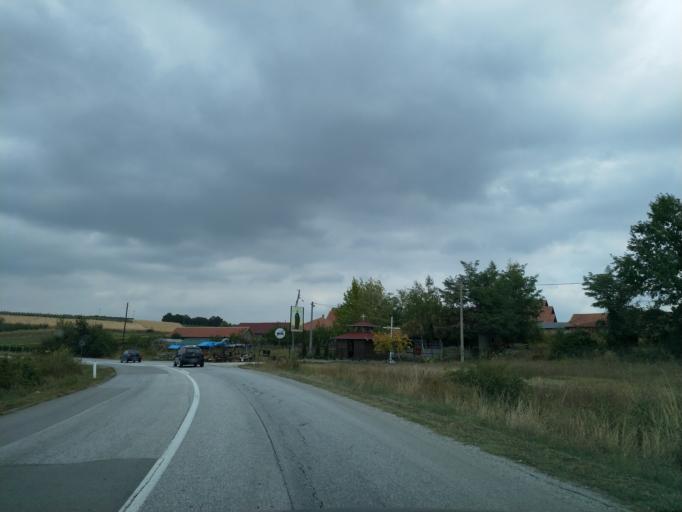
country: RS
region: Central Serbia
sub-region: Sumadijski Okrug
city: Topola
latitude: 44.1884
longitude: 20.7362
